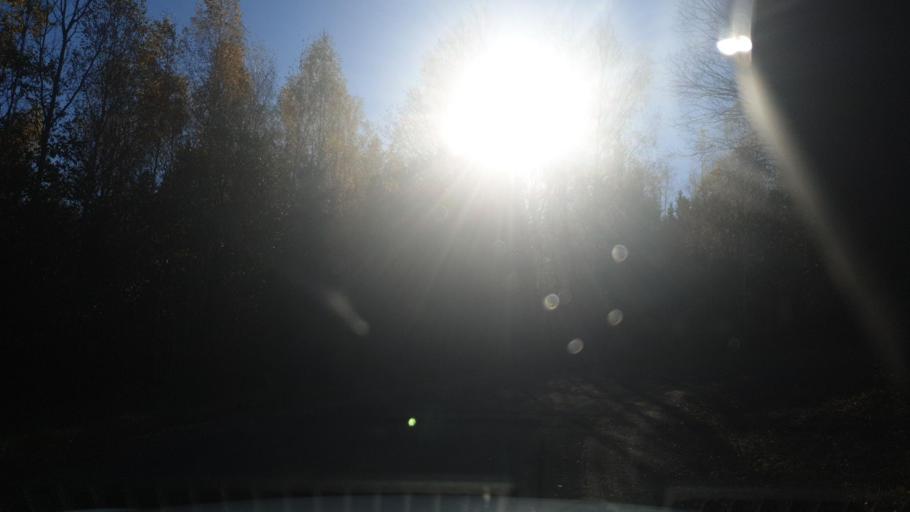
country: SE
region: Vaermland
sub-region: Grums Kommun
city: Grums
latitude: 59.4757
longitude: 12.9289
